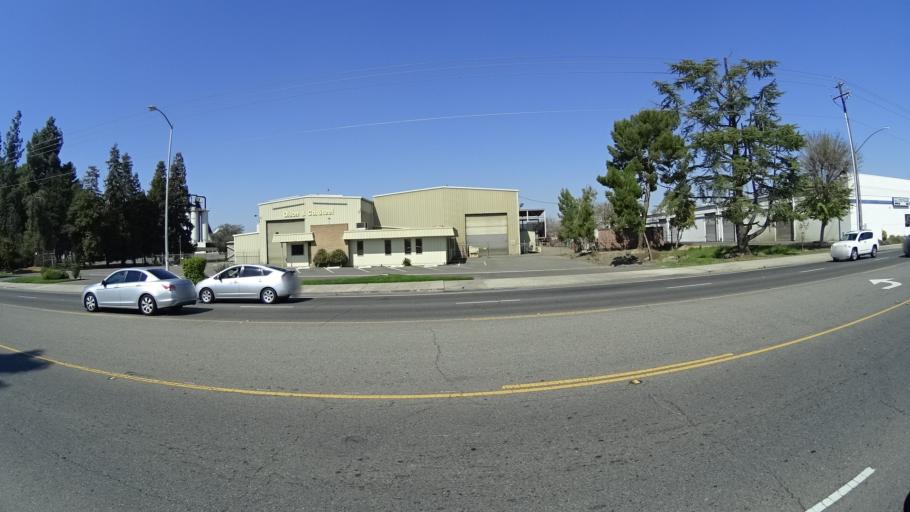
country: US
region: California
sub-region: Fresno County
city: West Park
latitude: 36.7935
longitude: -119.8549
